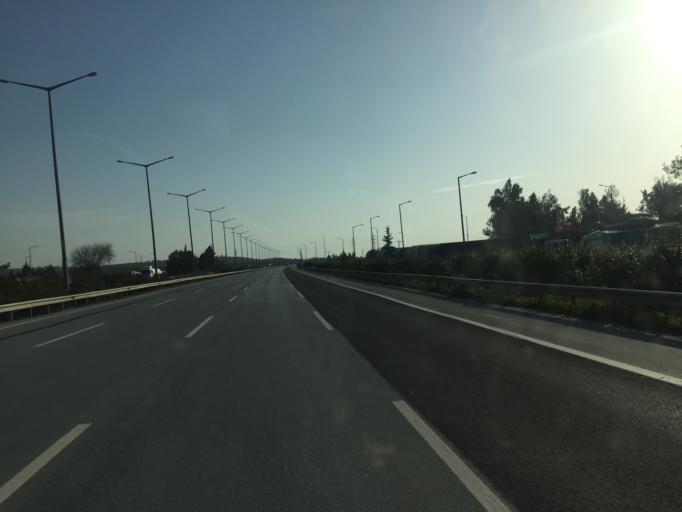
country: TR
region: Mersin
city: Yenice
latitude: 37.0235
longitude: 35.0615
